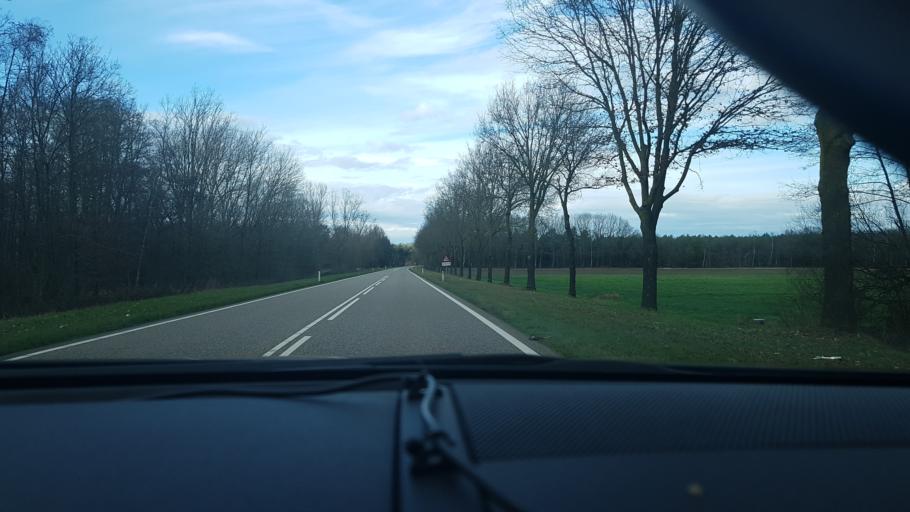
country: NL
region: Limburg
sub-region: Gemeente Beesel
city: Reuver
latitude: 51.3135
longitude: 6.0511
